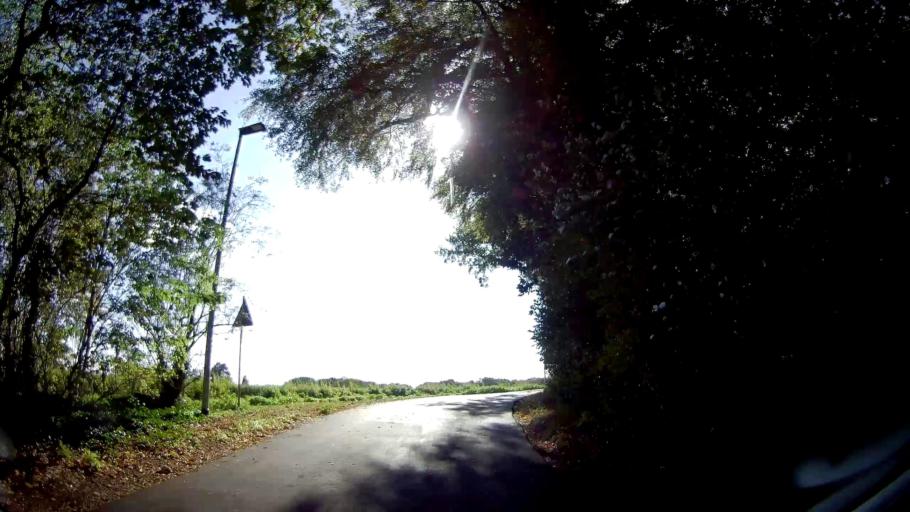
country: DE
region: North Rhine-Westphalia
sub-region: Regierungsbezirk Dusseldorf
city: Hunxe
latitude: 51.6321
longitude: 6.7662
